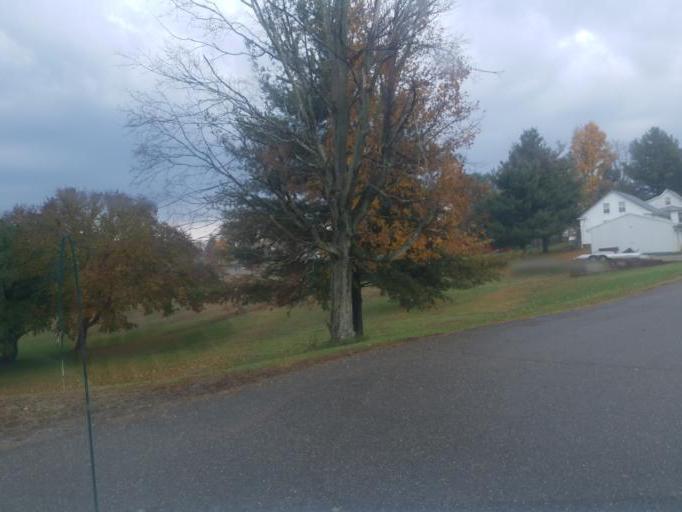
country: US
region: Ohio
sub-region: Morgan County
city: McConnelsville
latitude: 39.4894
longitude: -81.8695
